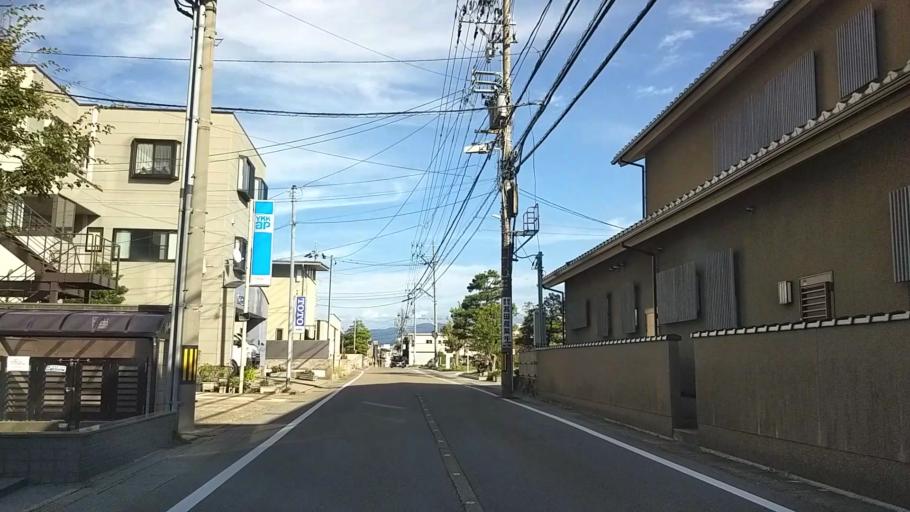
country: JP
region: Ishikawa
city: Kanazawa-shi
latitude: 36.5762
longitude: 136.6366
